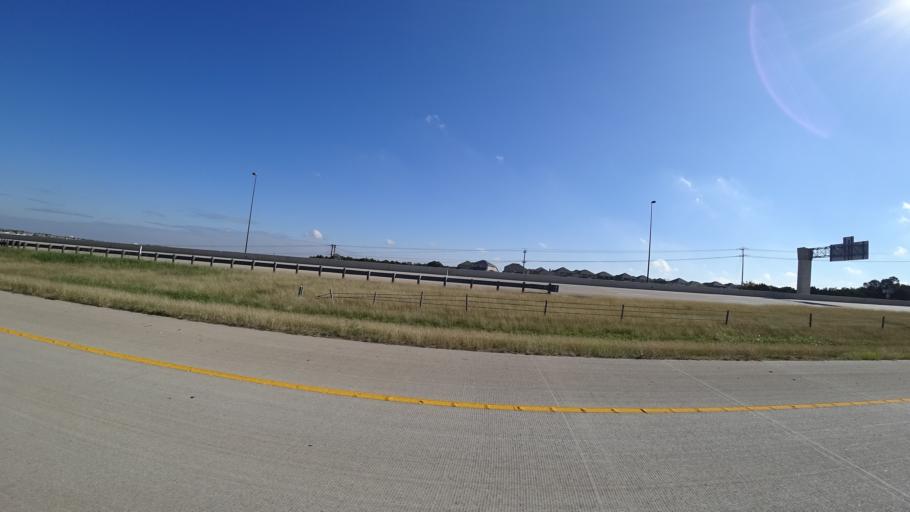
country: US
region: Texas
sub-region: Williamson County
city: Cedar Park
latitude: 30.4957
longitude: -97.8029
